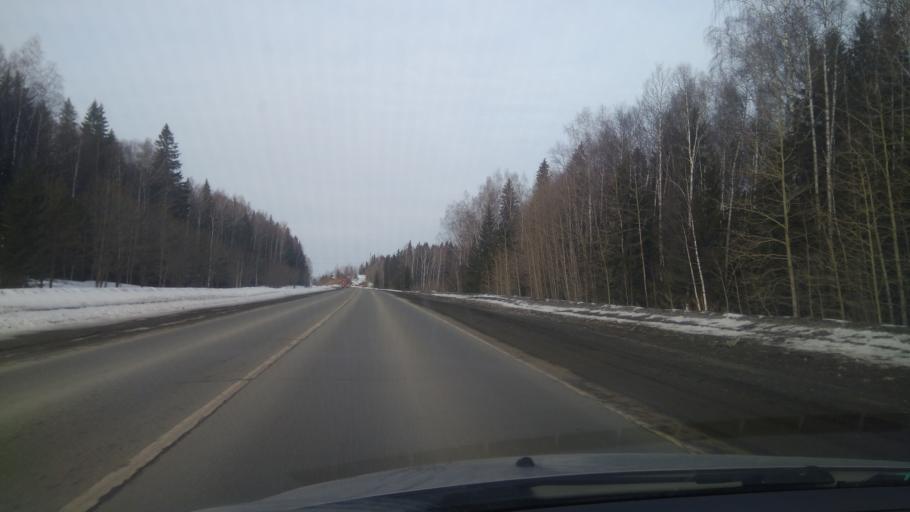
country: RU
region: Sverdlovsk
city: Bisert'
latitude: 56.8291
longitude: 59.0911
